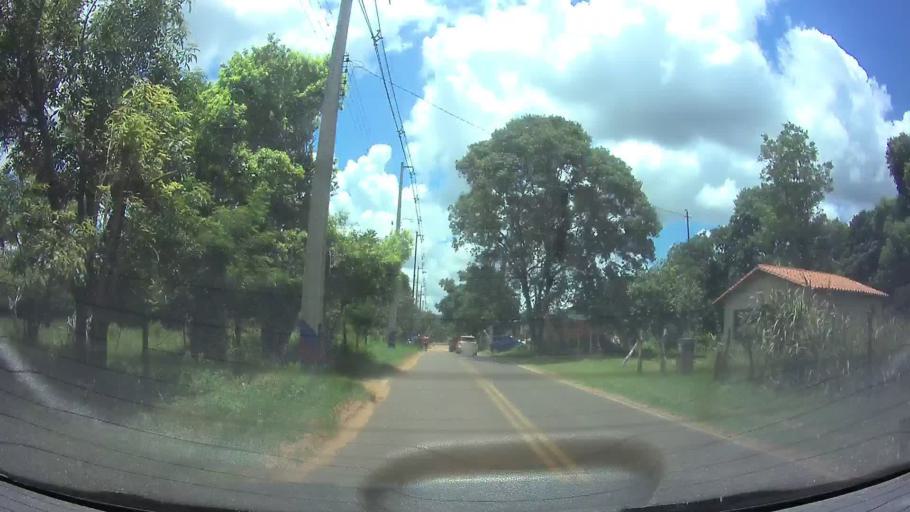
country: PY
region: Central
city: Capiata
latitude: -25.3268
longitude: -57.4248
